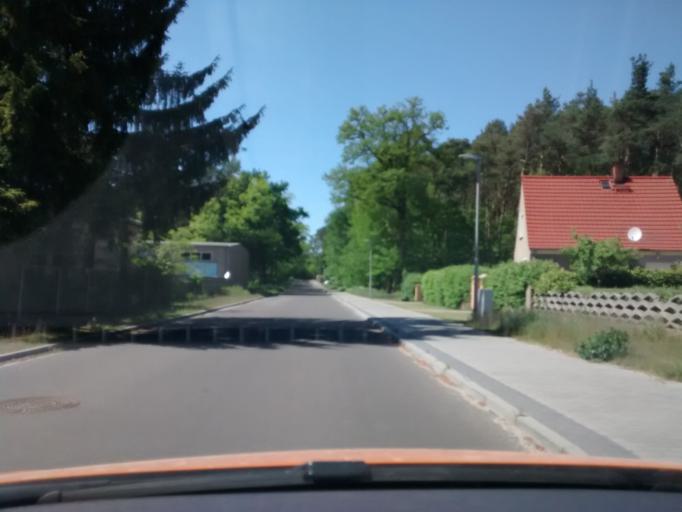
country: DE
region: Brandenburg
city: Wendisch Rietz
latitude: 52.2197
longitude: 14.0035
